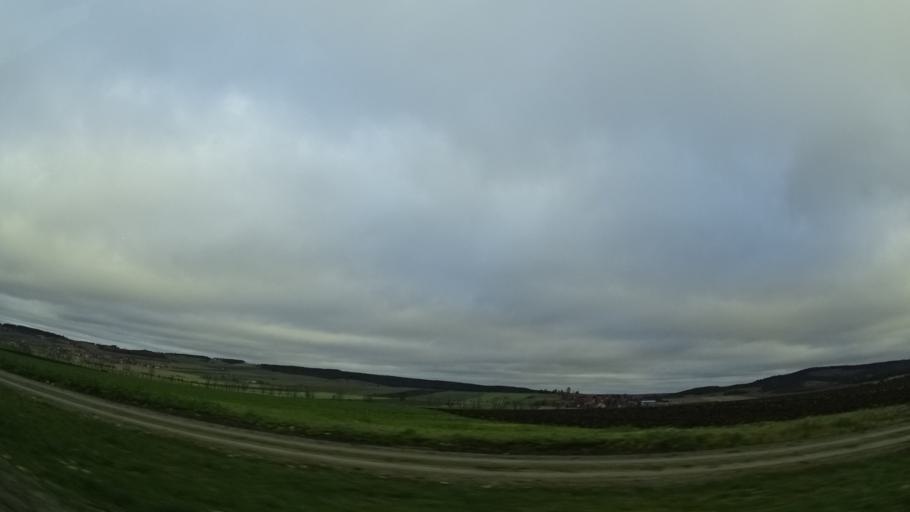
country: DE
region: Thuringia
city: Rottenbach
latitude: 50.7403
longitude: 11.1521
